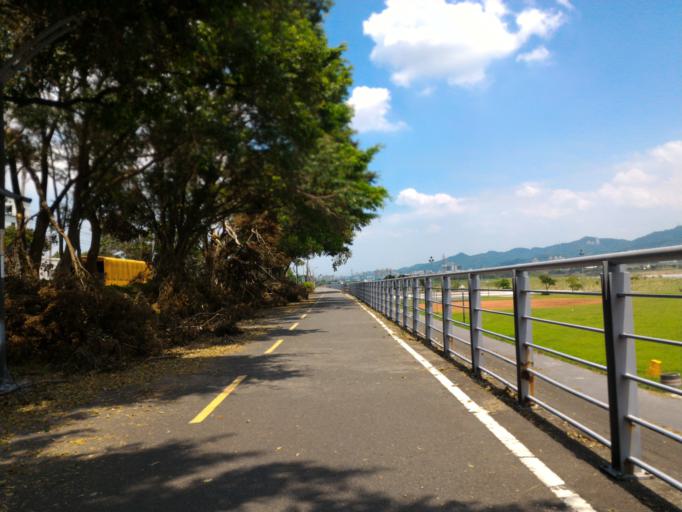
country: TW
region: Taipei
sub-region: Taipei
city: Banqiao
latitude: 24.9696
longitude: 121.4095
